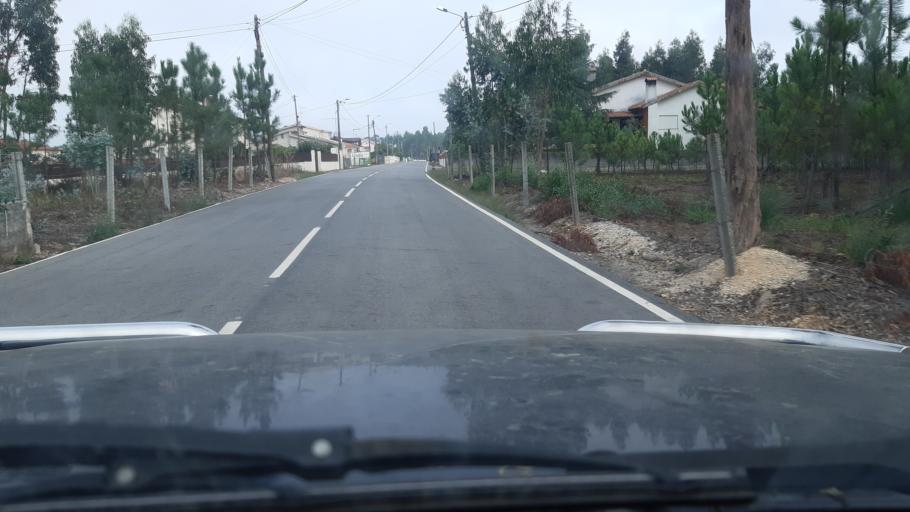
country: PT
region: Aveiro
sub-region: Agueda
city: Agueda
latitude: 40.5820
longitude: -8.4558
